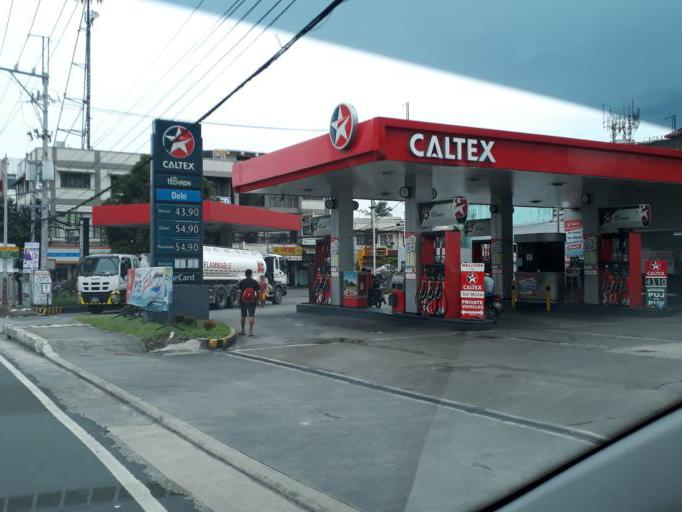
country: PH
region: Calabarzon
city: Del Monte
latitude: 14.6398
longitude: 121.0105
